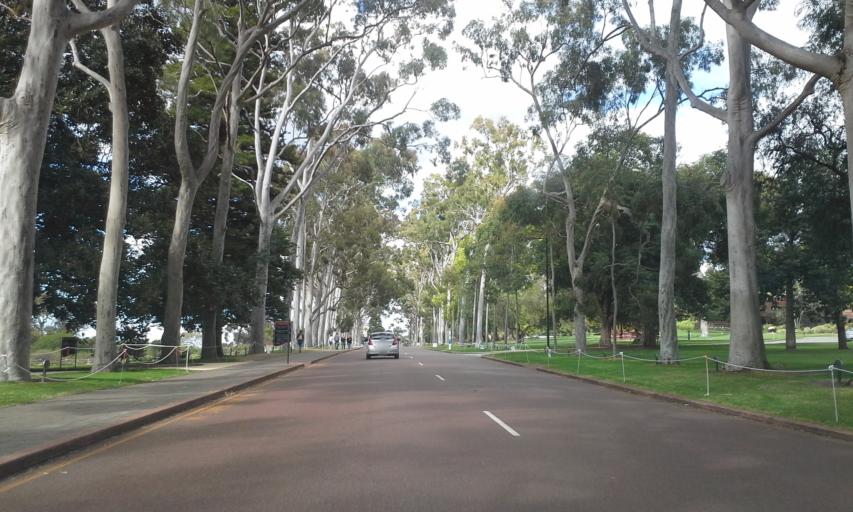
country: AU
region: Western Australia
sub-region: City of Perth
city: West Perth
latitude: -31.9564
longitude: 115.8443
